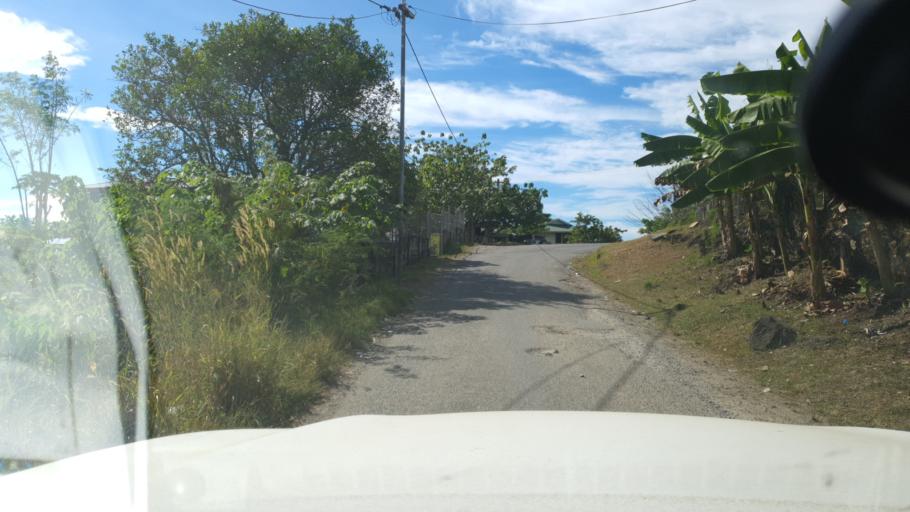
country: SB
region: Guadalcanal
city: Honiara
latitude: -9.4372
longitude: 159.9534
